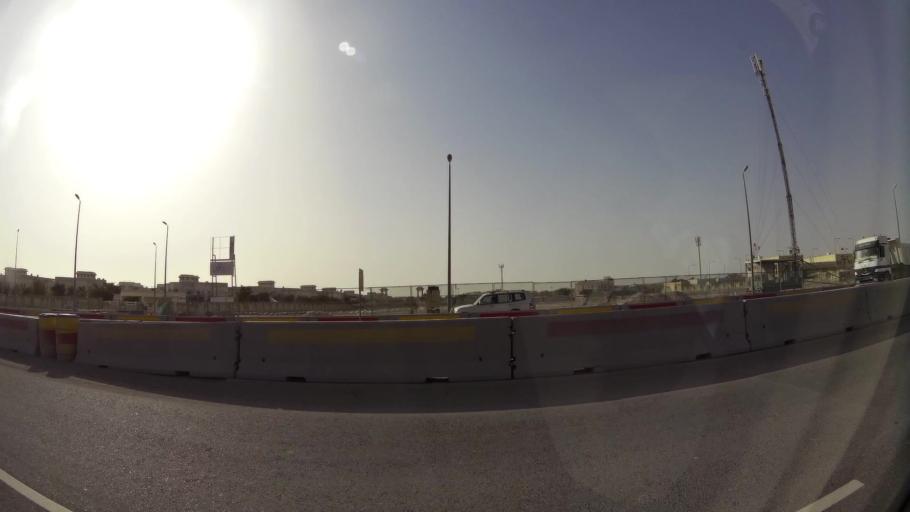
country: QA
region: Baladiyat ar Rayyan
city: Ar Rayyan
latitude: 25.3238
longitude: 51.4229
